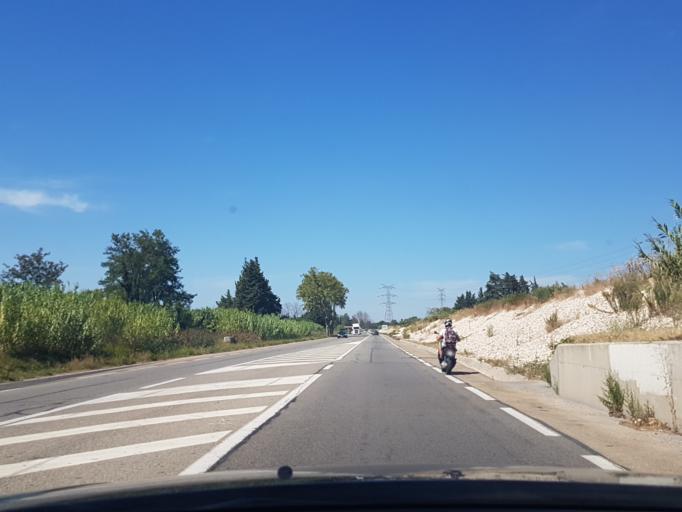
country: FR
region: Provence-Alpes-Cote d'Azur
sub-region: Departement des Bouches-du-Rhone
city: Rognonas
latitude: 43.9083
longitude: 4.8120
